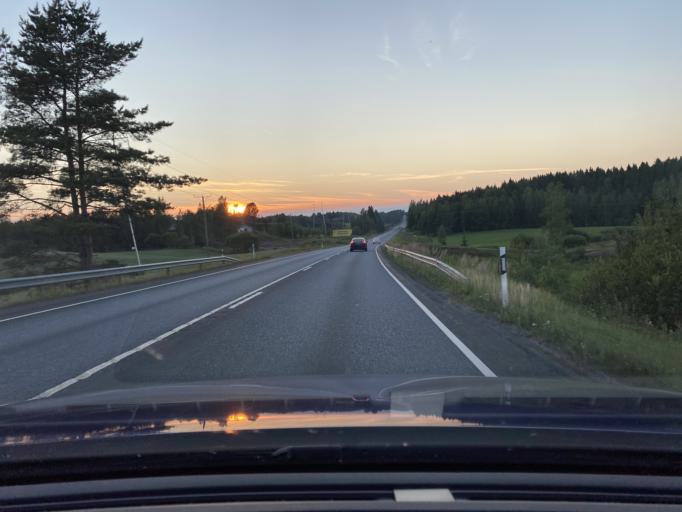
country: FI
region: Pirkanmaa
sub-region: Luoteis-Pirkanmaa
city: Ikaalinen
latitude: 61.8054
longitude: 22.9663
